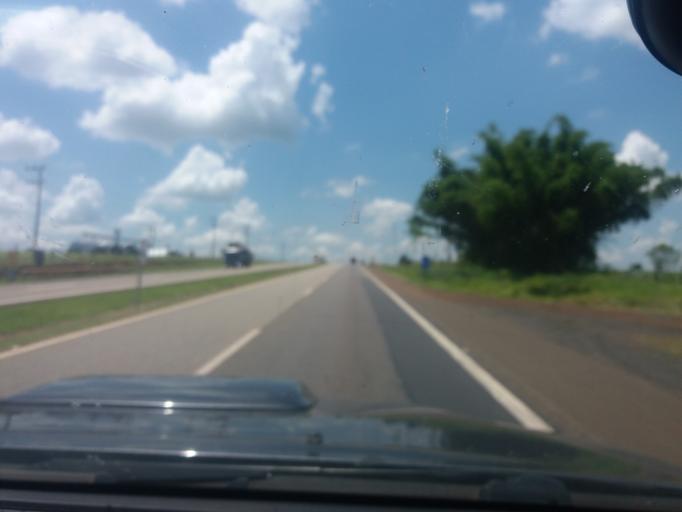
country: BR
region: Sao Paulo
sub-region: Itapetininga
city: Itapetininga
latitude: -23.5294
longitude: -47.9647
